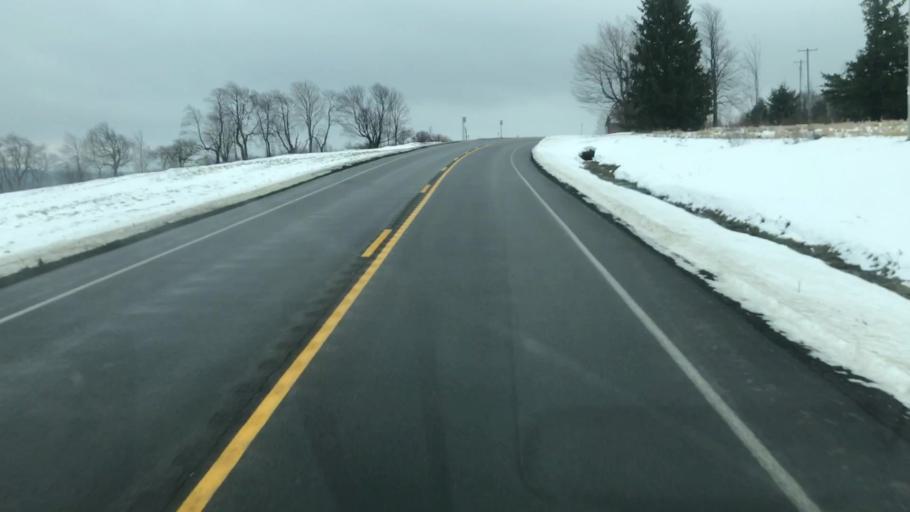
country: US
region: New York
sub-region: Cayuga County
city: Moravia
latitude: 42.7702
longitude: -76.3328
